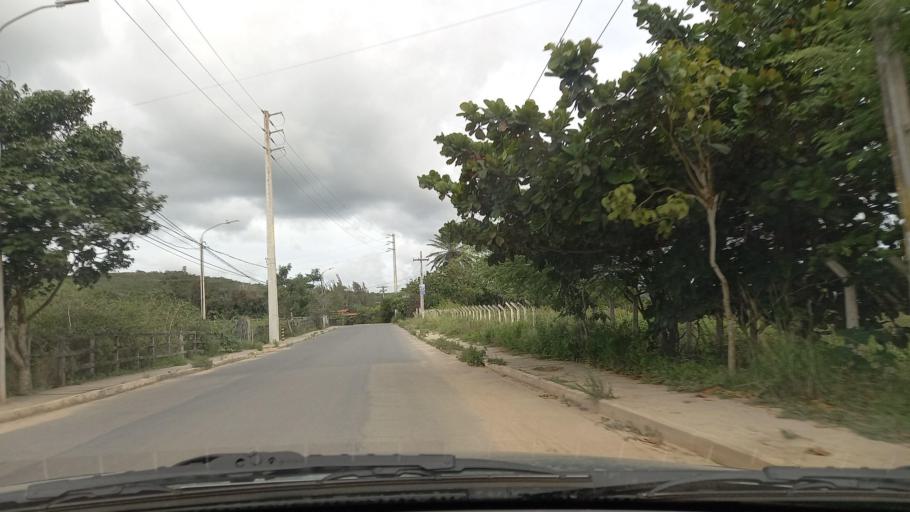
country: BR
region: Pernambuco
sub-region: Gravata
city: Gravata
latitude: -8.2063
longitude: -35.5581
